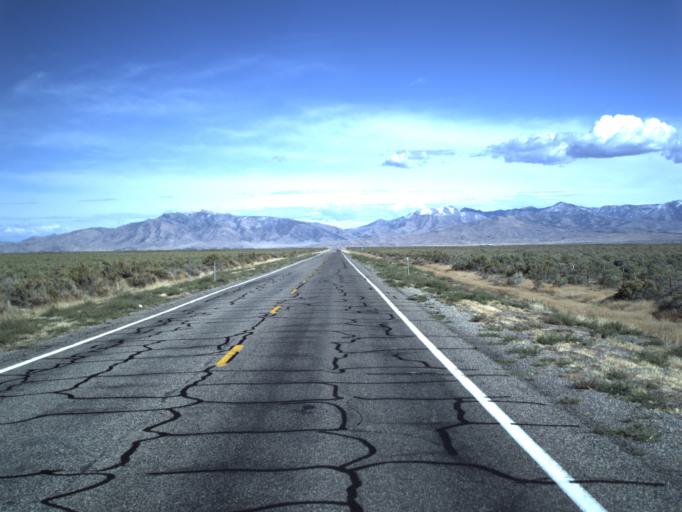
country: US
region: Utah
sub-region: Millard County
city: Delta
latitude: 39.3531
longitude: -112.5185
